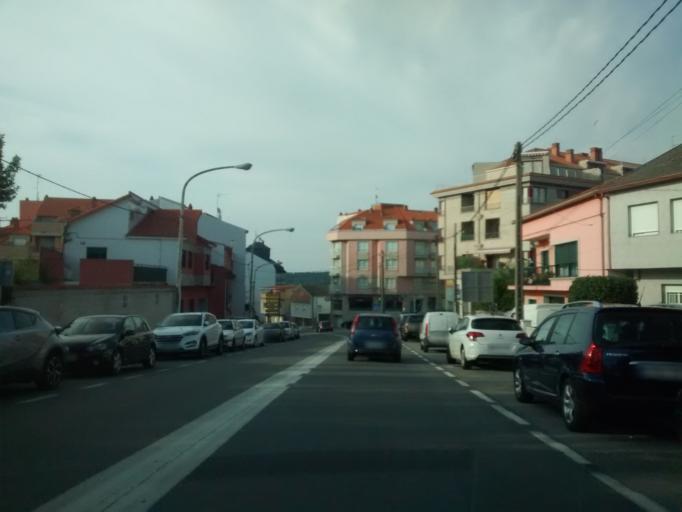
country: ES
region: Galicia
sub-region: Provincia de Pontevedra
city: Sanxenxo
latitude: 42.3931
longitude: -8.8292
